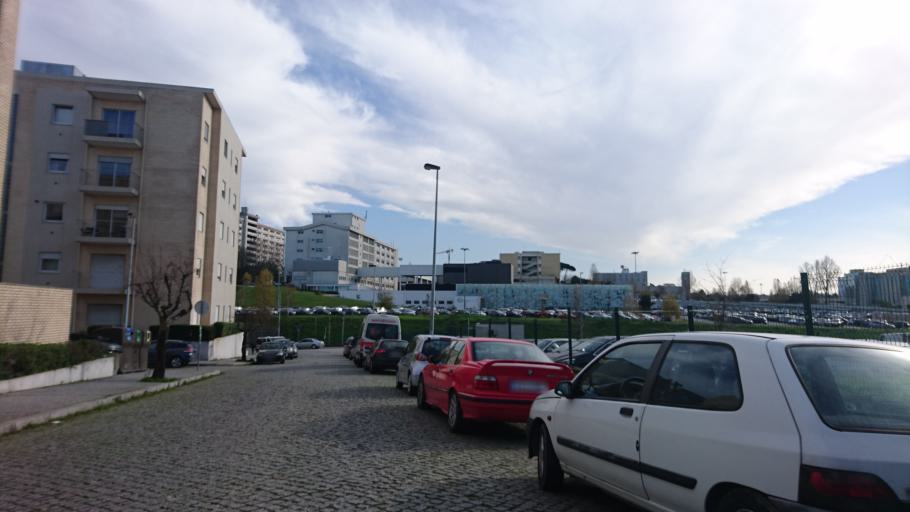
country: PT
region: Porto
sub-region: Matosinhos
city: Sao Mamede de Infesta
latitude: 41.1822
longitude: -8.6088
